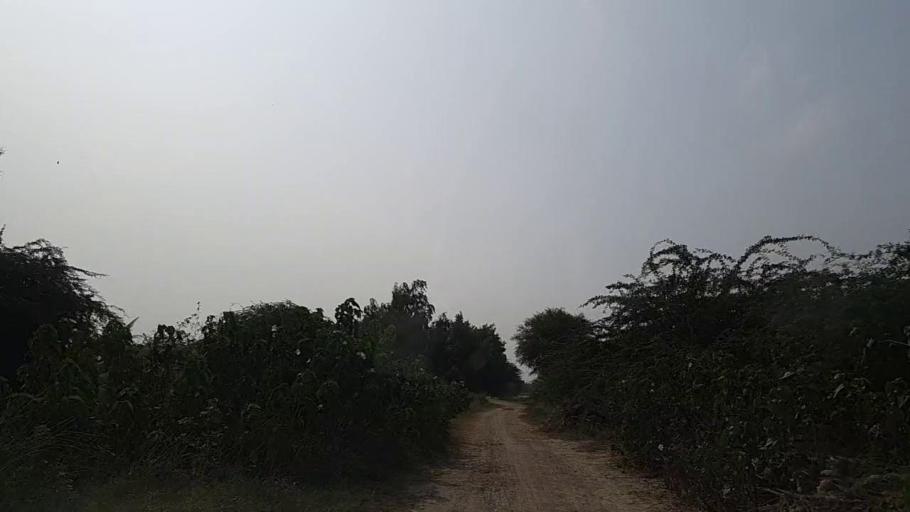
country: PK
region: Sindh
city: Mirpur Sakro
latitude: 24.6541
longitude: 67.7683
